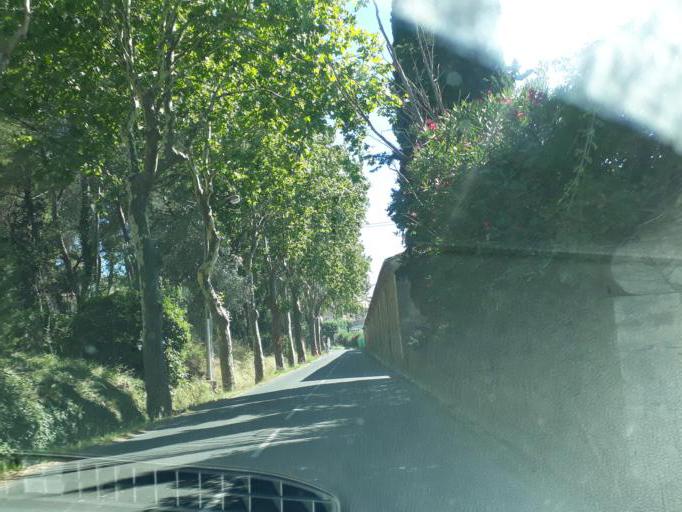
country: FR
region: Languedoc-Roussillon
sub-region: Departement de l'Herault
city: Castelnau-de-Guers
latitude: 43.4395
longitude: 3.4397
